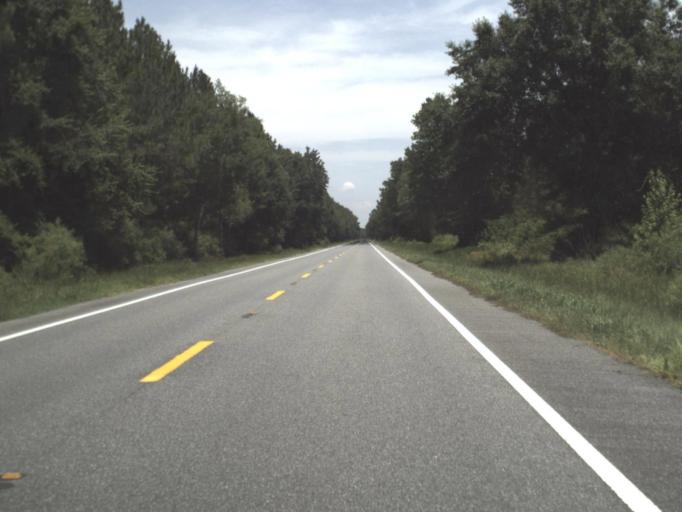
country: US
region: Florida
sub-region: Lafayette County
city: Mayo
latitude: 29.8981
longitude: -83.2970
